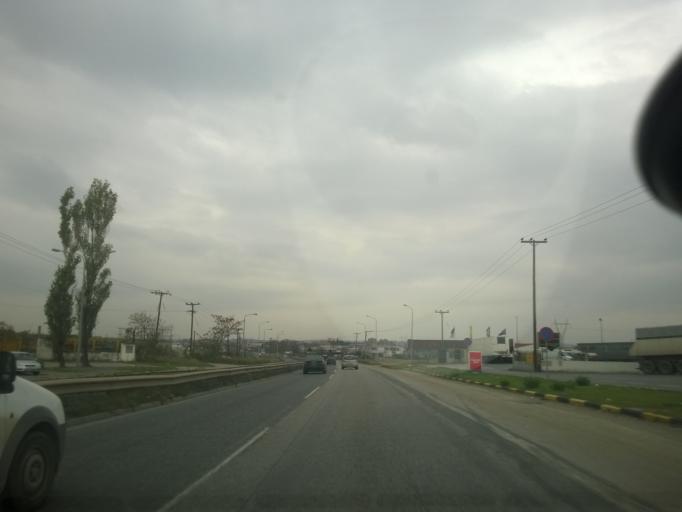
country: GR
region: Central Macedonia
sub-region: Nomos Thessalonikis
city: Sindos
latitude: 40.7050
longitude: 22.8103
